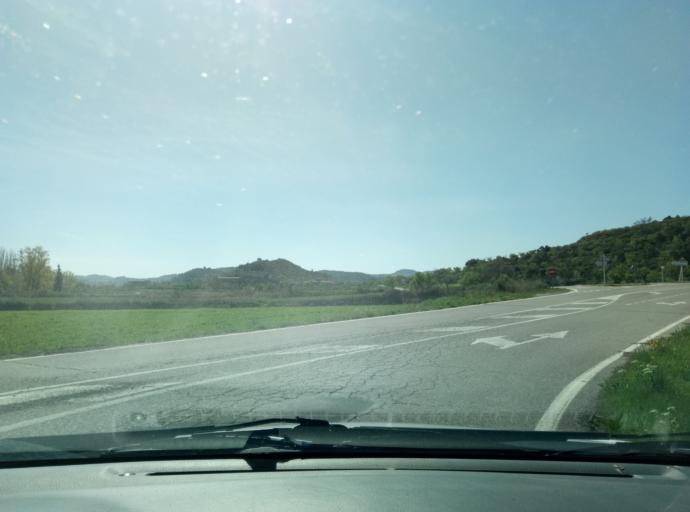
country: ES
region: Catalonia
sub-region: Provincia de Lleida
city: Vallbona de les Monges
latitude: 41.5507
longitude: 1.0317
